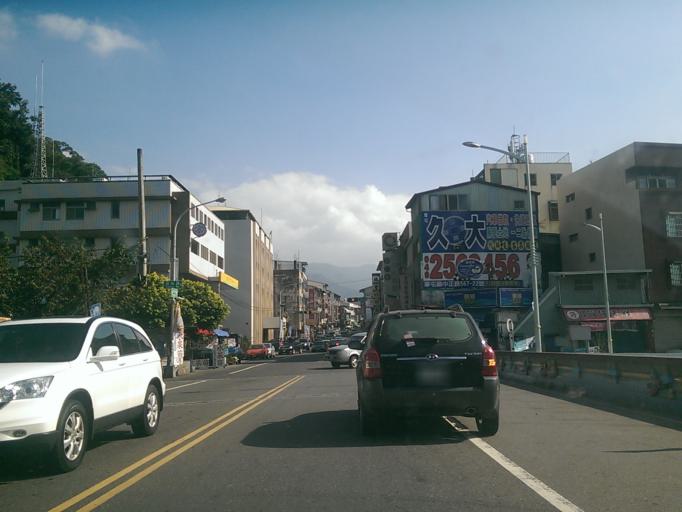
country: TW
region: Taiwan
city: Lugu
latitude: 23.8154
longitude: 120.8547
